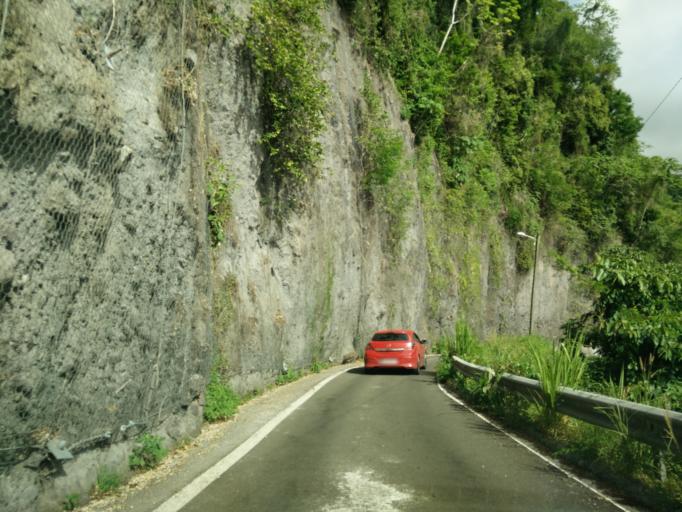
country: MQ
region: Martinique
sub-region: Martinique
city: Basse-Pointe
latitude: 14.8722
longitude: -61.1750
